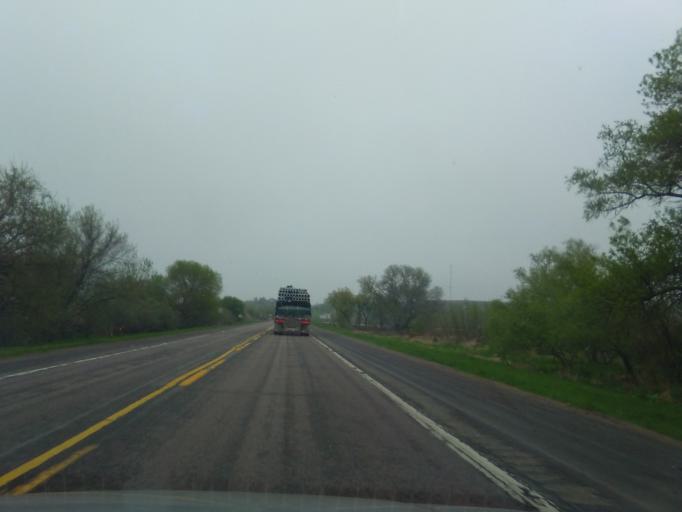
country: US
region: Nebraska
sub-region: Burt County
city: Oakland
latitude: 41.8123
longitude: -96.4751
